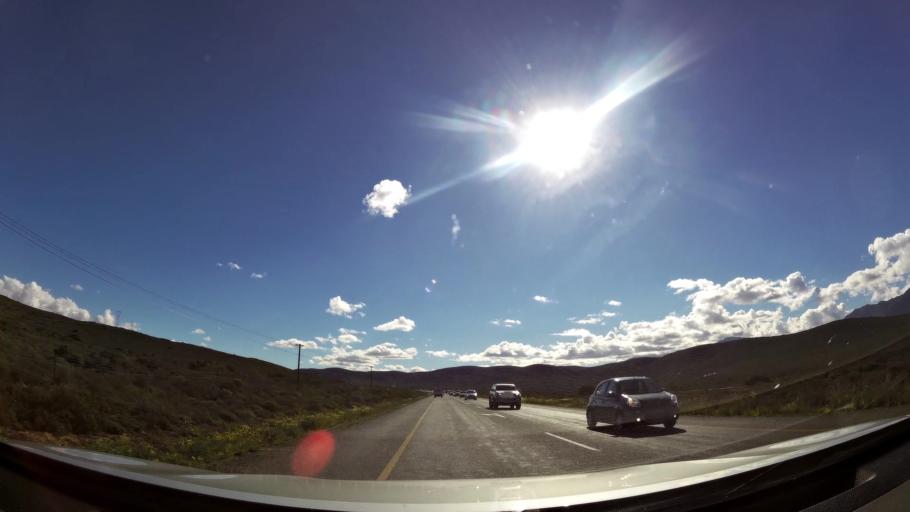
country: ZA
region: Western Cape
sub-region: Cape Winelands District Municipality
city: Worcester
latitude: -33.7422
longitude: 19.6952
